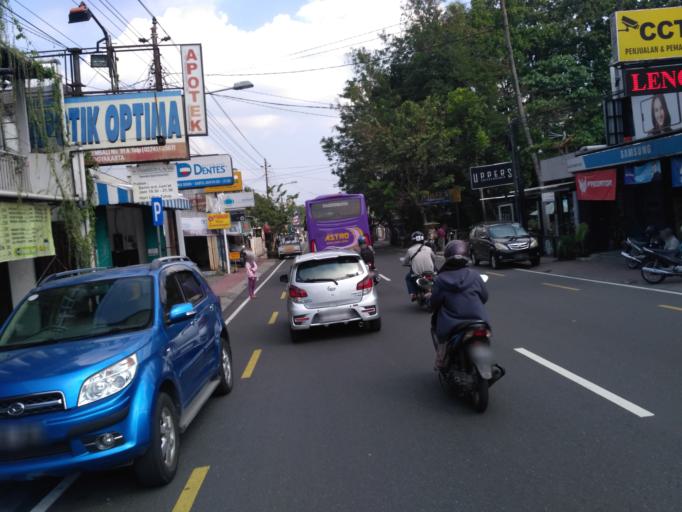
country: ID
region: Daerah Istimewa Yogyakarta
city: Yogyakarta
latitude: -7.7589
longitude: 110.3696
